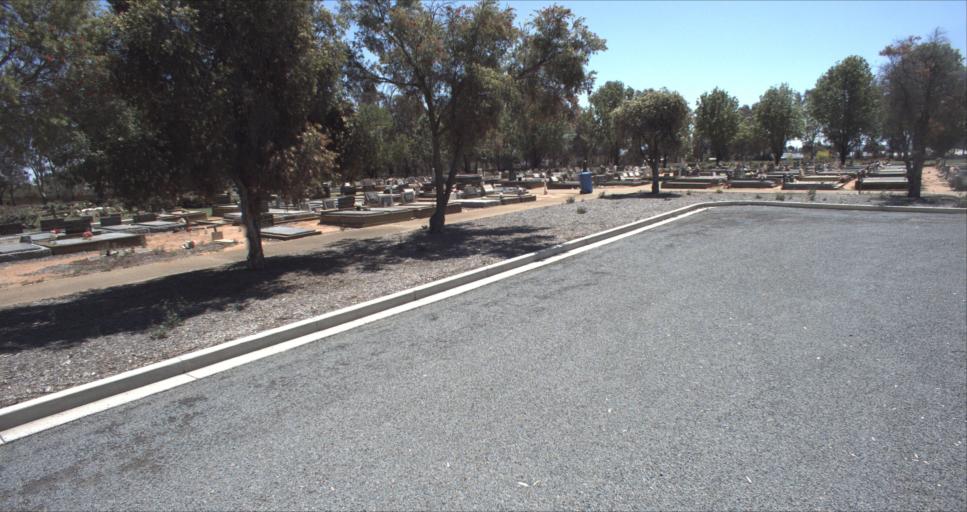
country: AU
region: New South Wales
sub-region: Leeton
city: Leeton
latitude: -34.5327
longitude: 146.3980
